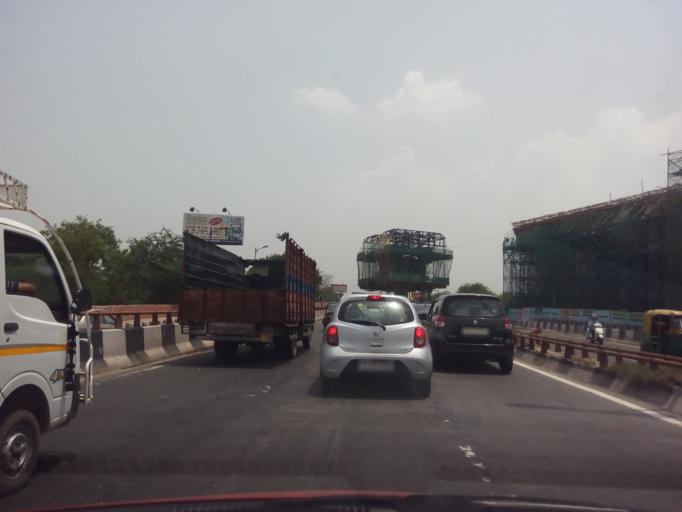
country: IN
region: NCT
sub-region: North West Delhi
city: Pitampura
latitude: 28.6339
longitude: 77.1314
